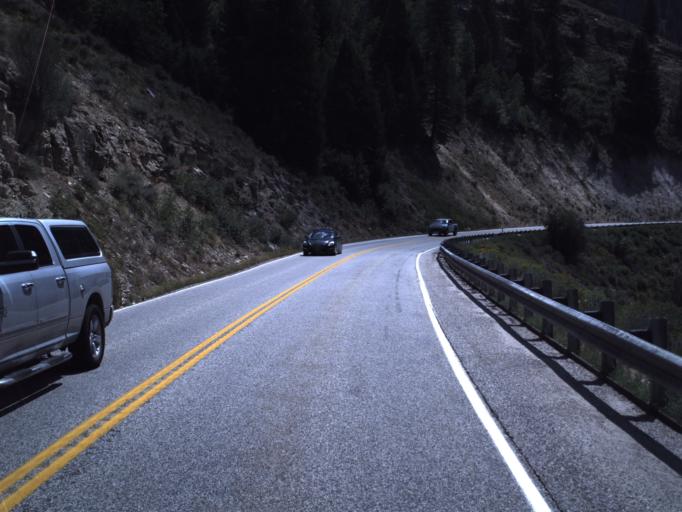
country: US
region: Utah
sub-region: Cache County
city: North Logan
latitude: 41.8269
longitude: -111.6014
